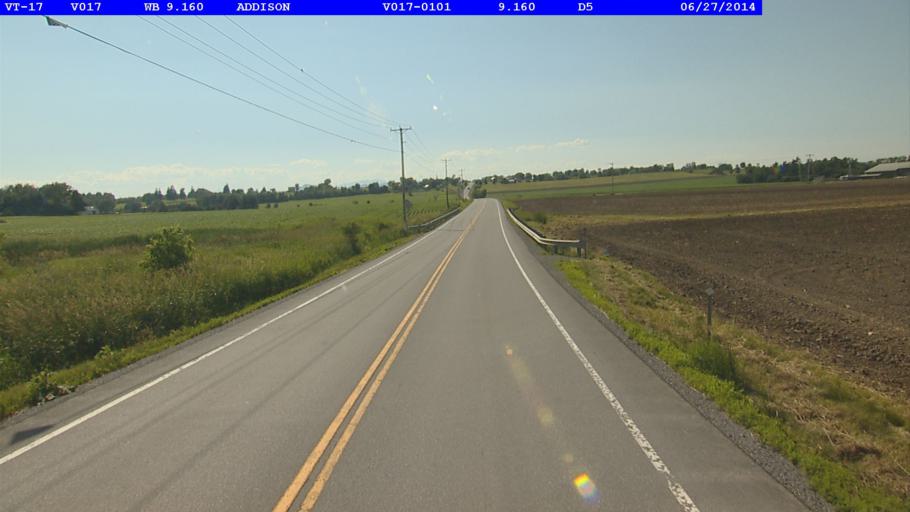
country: US
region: Vermont
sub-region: Addison County
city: Vergennes
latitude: 44.0848
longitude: -73.2879
